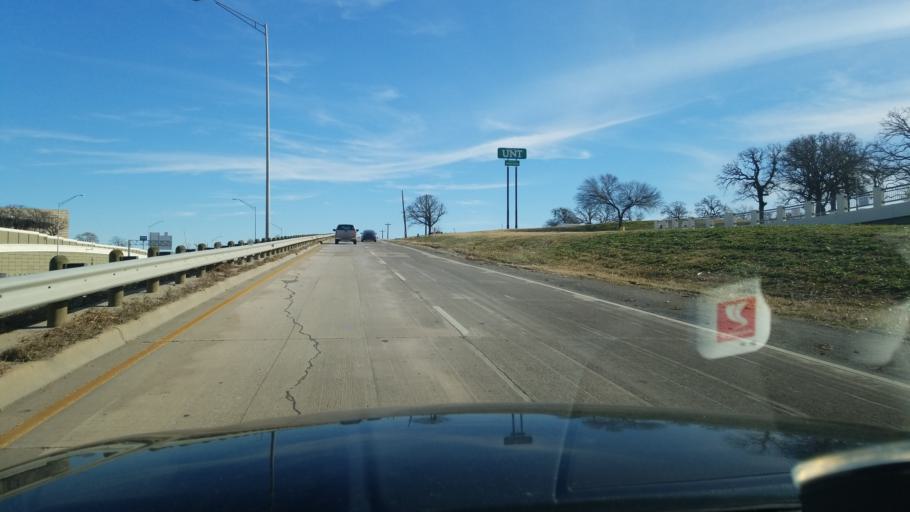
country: US
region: Texas
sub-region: Denton County
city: Denton
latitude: 33.2063
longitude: -97.1578
